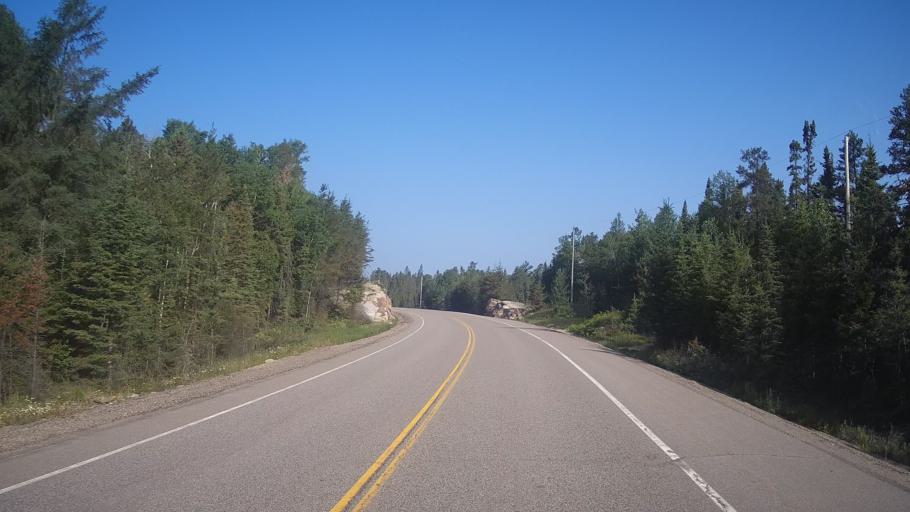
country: CA
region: Ontario
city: Rayside-Balfour
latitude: 46.7295
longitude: -81.5815
